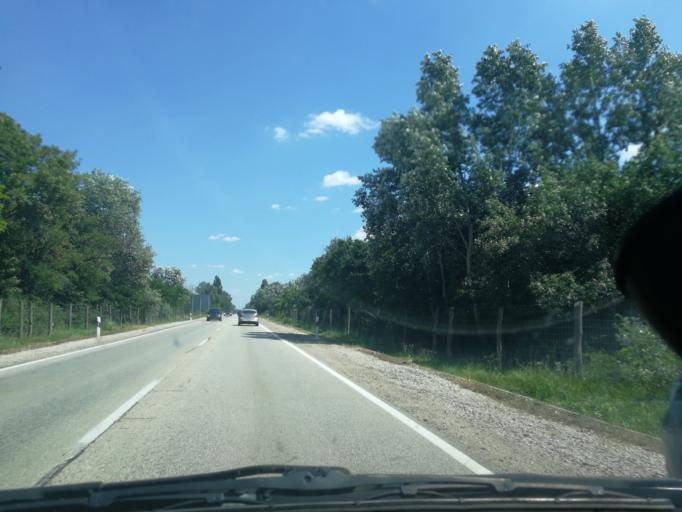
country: HU
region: Fejer
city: Pakozd
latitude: 47.1888
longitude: 18.5167
